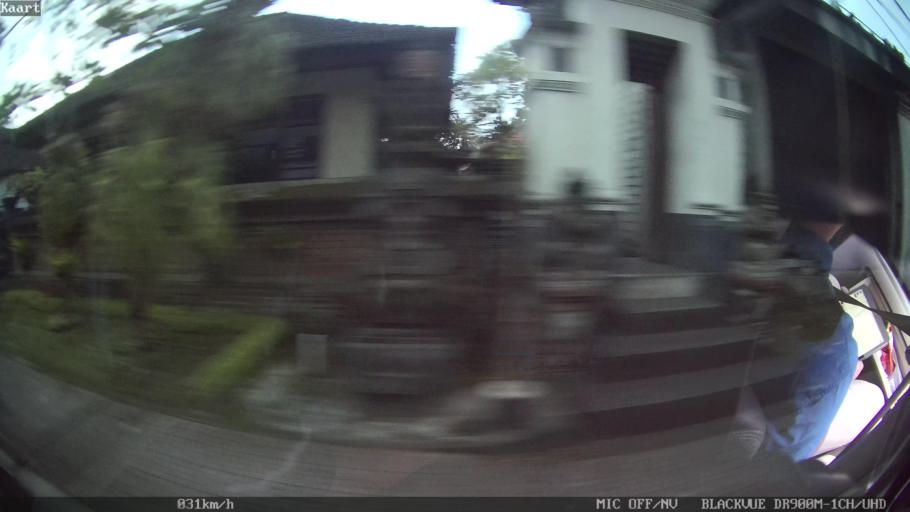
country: ID
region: Bali
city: Bunutan
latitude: -8.4825
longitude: 115.2466
